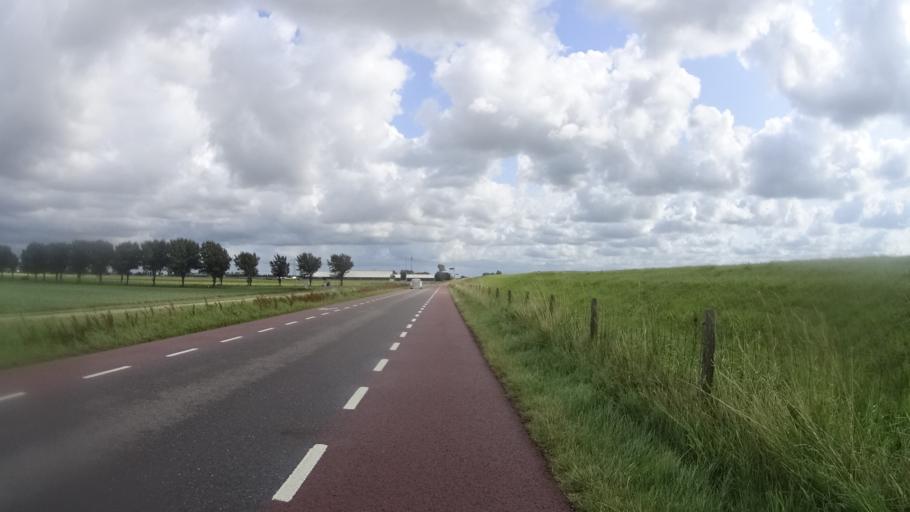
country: NL
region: North Holland
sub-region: Gemeente Schagen
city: Schagen
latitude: 52.8258
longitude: 4.8182
